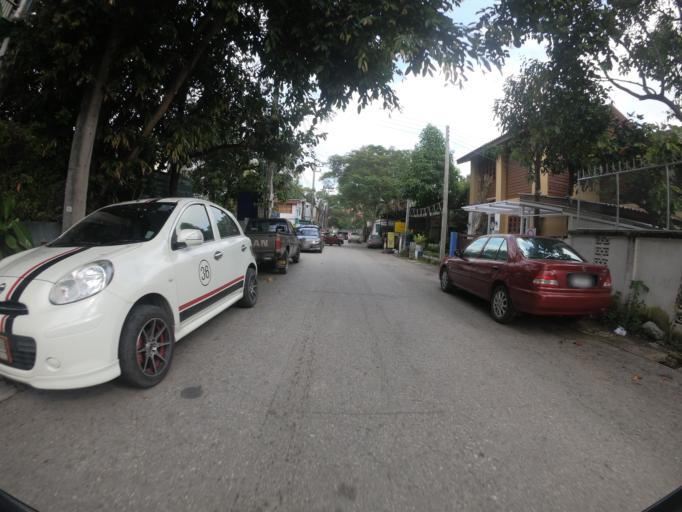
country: TH
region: Chiang Mai
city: Chiang Mai
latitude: 18.7925
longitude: 98.9539
